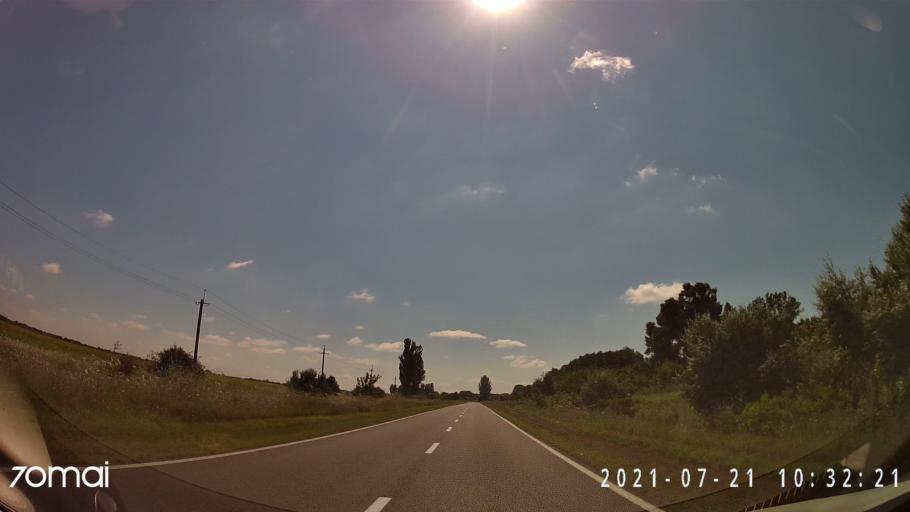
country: RO
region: Tulcea
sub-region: Oras Isaccea
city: Isaccea
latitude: 45.3022
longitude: 28.4217
